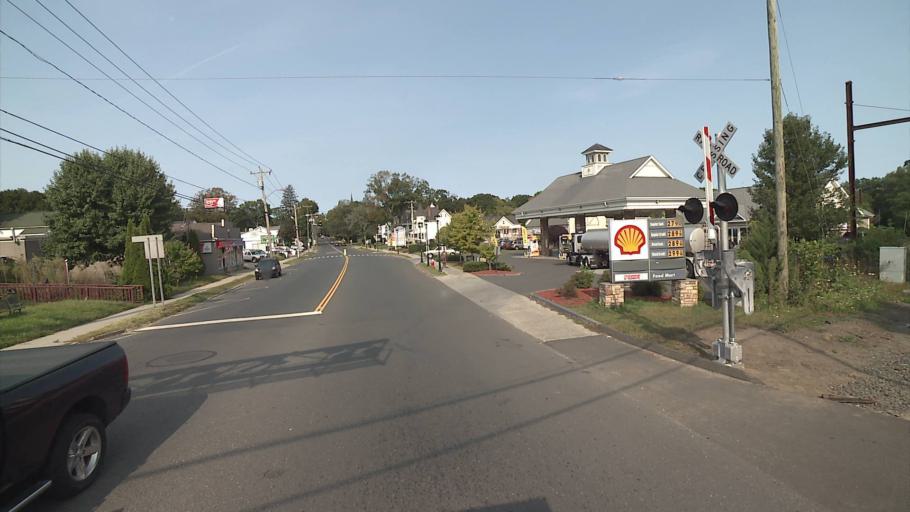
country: US
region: Connecticut
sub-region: Fairfield County
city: Bethel
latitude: 41.3713
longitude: -73.4148
